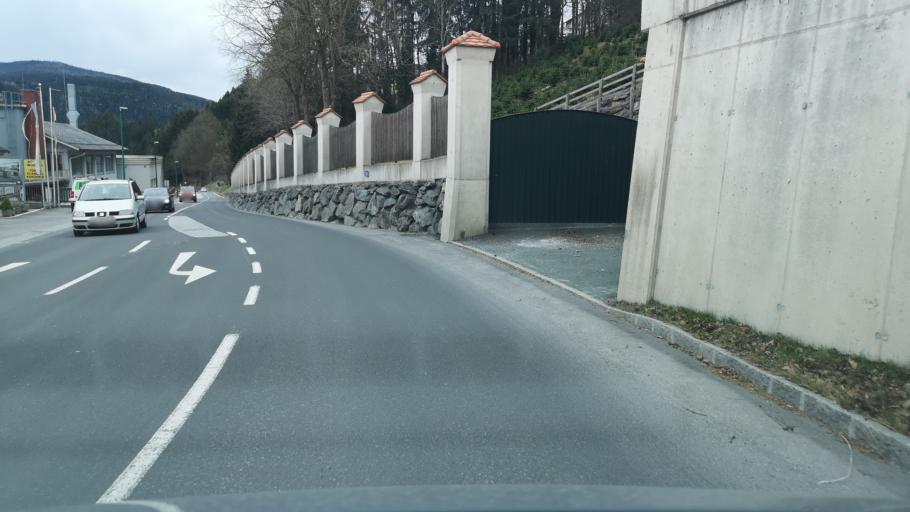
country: AT
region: Styria
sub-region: Politischer Bezirk Weiz
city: Birkfeld
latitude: 47.3531
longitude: 15.6947
